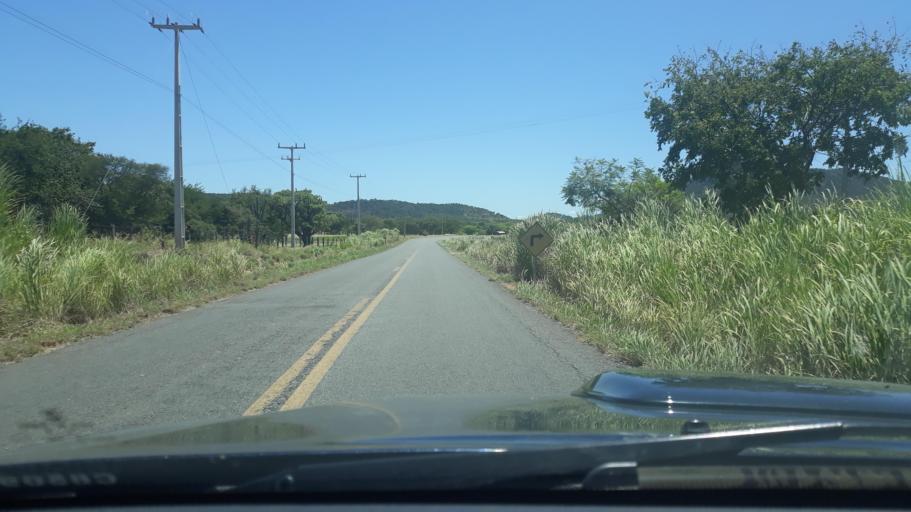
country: BR
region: Bahia
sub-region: Guanambi
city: Guanambi
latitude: -14.1543
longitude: -42.8241
